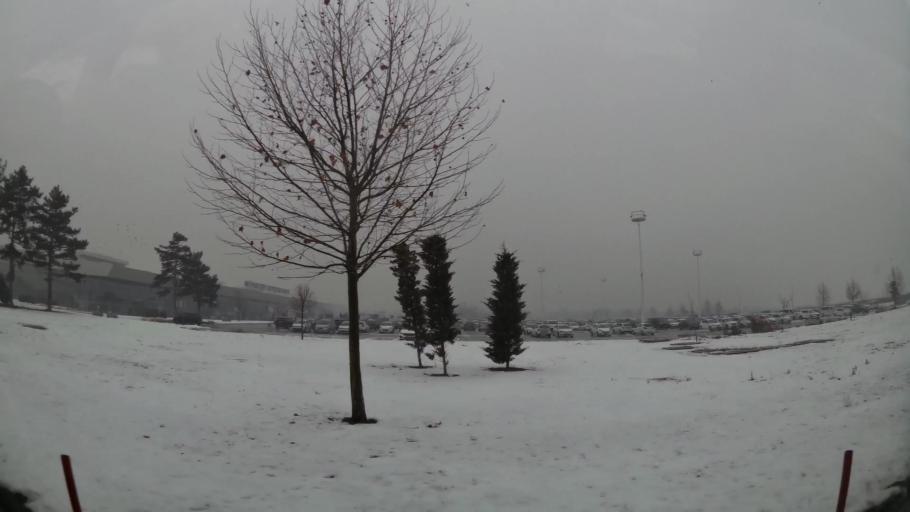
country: MK
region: Petrovec
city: Petrovec
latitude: 41.9597
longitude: 21.6290
